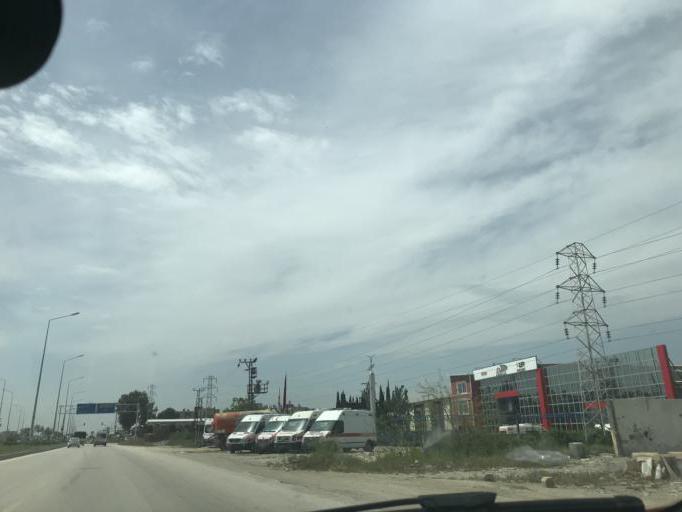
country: TR
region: Adana
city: Yuregir
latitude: 36.9821
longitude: 35.4338
